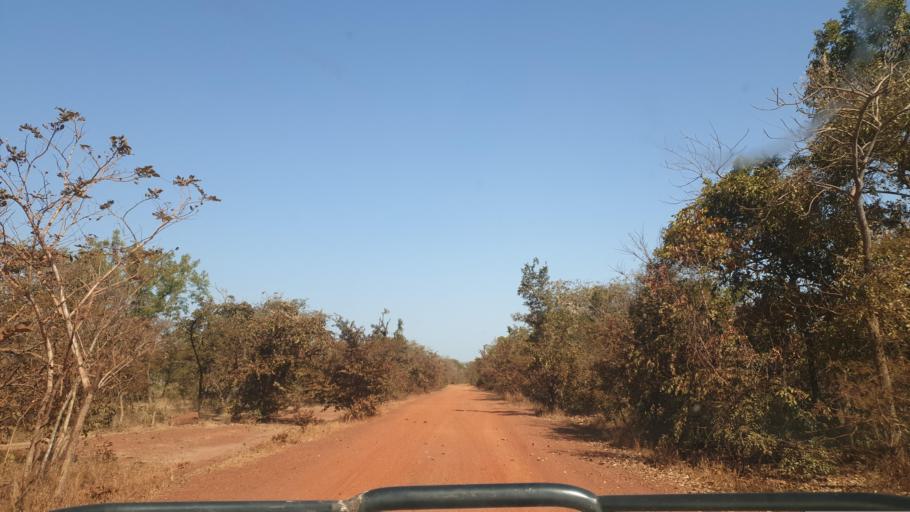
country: ML
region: Koulikoro
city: Dioila
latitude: 11.8503
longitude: -6.9788
